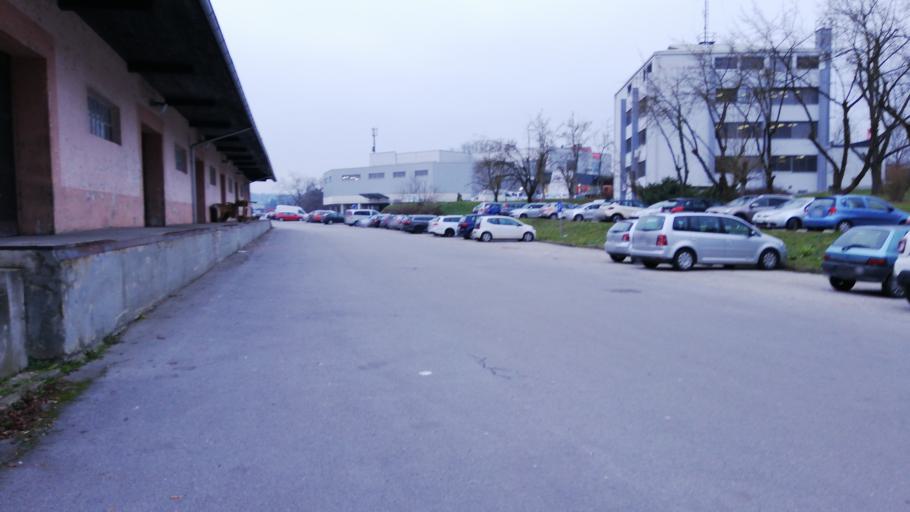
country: SI
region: Novo Mesto
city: Novo Mesto
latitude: 45.8114
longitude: 15.1554
